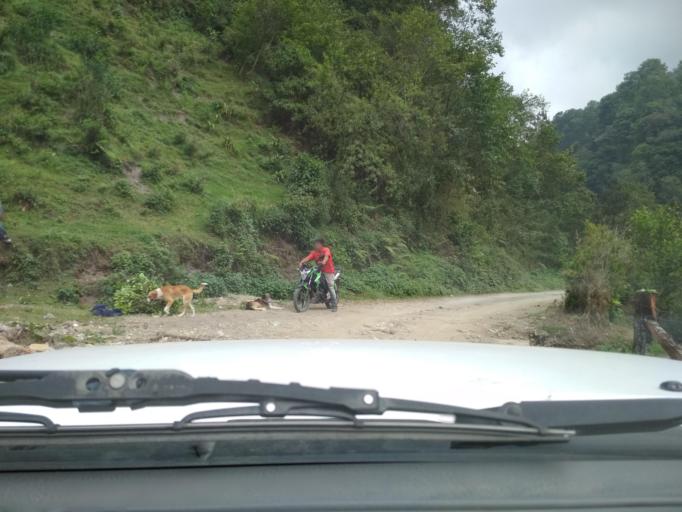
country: MX
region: Veracruz
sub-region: La Perla
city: Metlac Hernandez (Metlac Primero)
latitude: 18.9812
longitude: -97.1352
